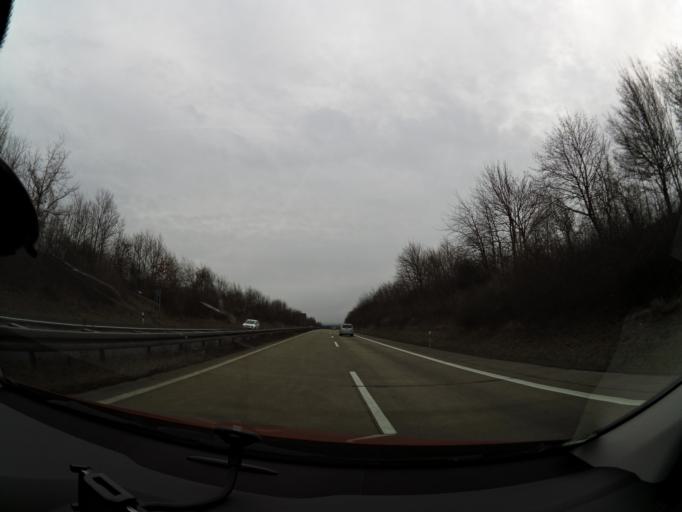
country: DE
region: Lower Saxony
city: Schladen
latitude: 52.0010
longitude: 10.5480
